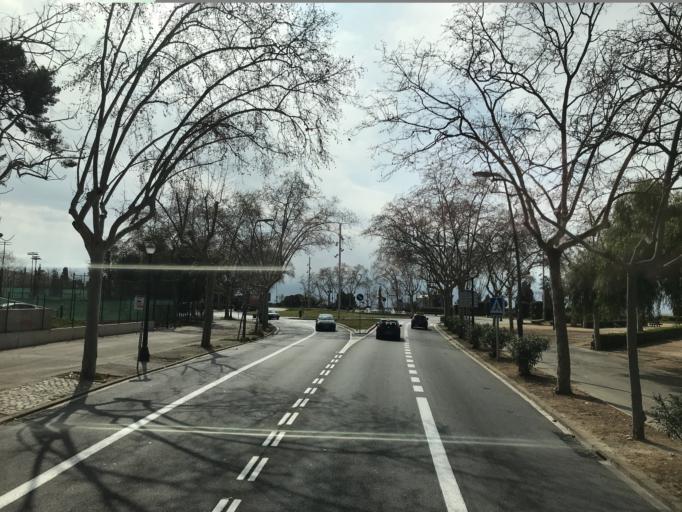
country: ES
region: Catalonia
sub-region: Provincia de Barcelona
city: Sants-Montjuic
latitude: 41.3681
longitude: 2.1452
